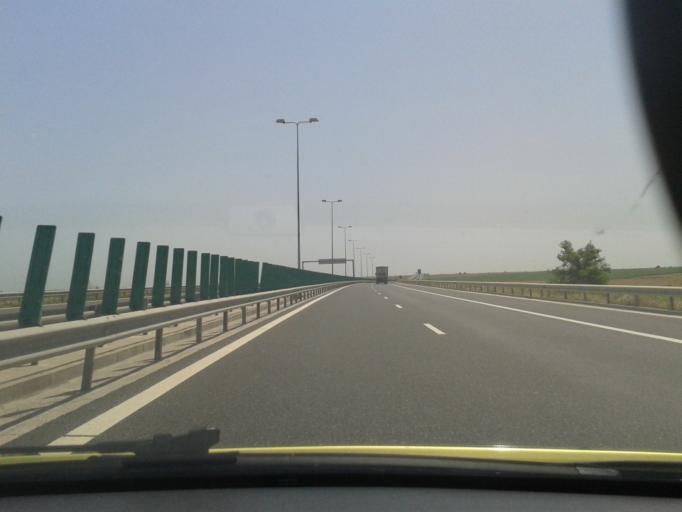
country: RO
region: Constanta
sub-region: Municipiul Constanta
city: Palazu Mare
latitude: 44.2101
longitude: 28.5530
